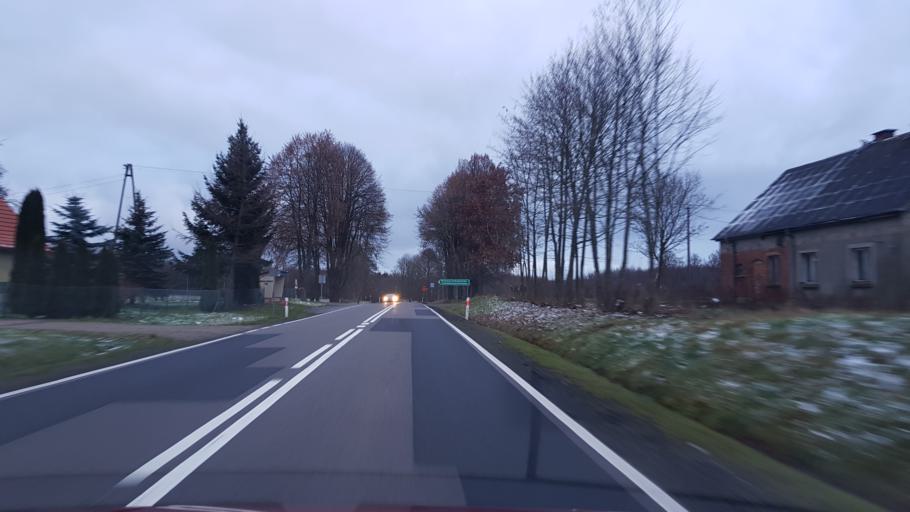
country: PL
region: Pomeranian Voivodeship
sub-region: Powiat bytowski
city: Tuchomie
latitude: 54.0891
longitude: 17.3086
